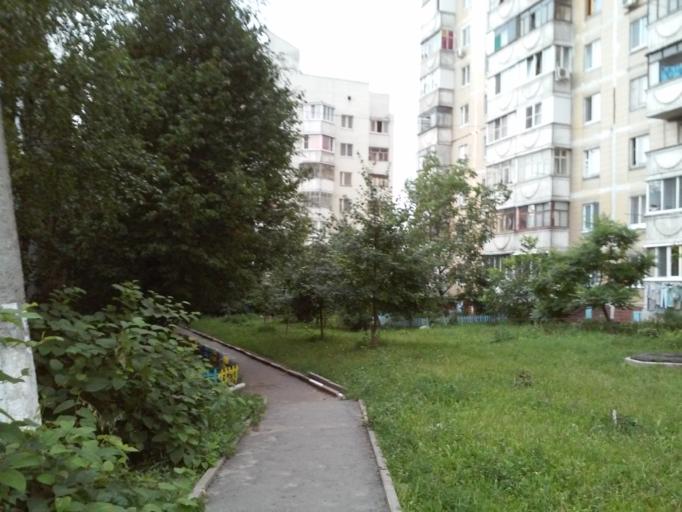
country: RU
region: Belgorod
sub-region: Belgorodskiy Rayon
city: Belgorod
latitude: 50.5679
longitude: 36.5757
